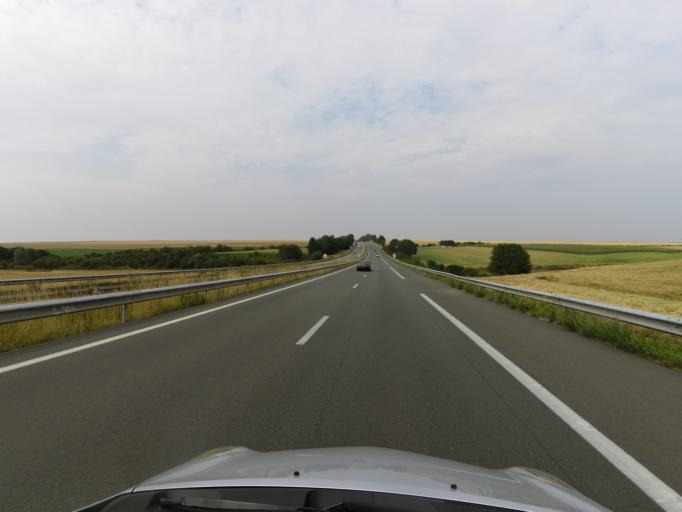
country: FR
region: Nord-Pas-de-Calais
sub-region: Departement du Nord
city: Gouzeaucourt
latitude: 50.0505
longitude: 3.1778
